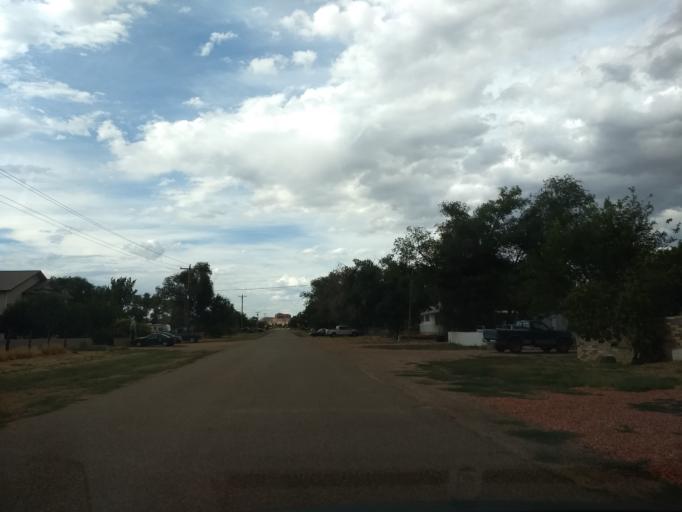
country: US
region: Arizona
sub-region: Coconino County
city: Fredonia
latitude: 36.9494
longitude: -112.5243
